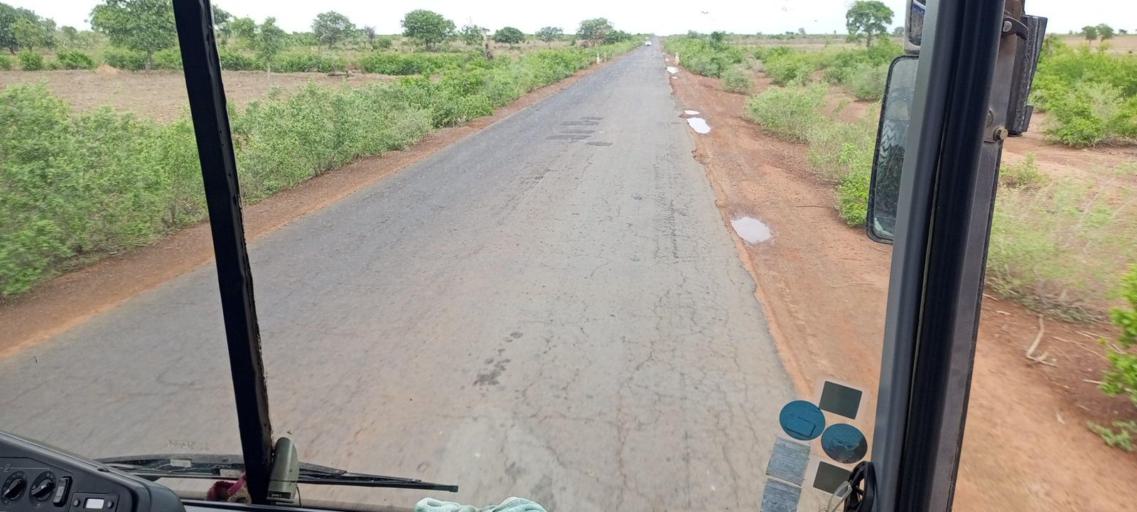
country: ML
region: Segou
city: Bla
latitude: 12.7112
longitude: -5.7245
